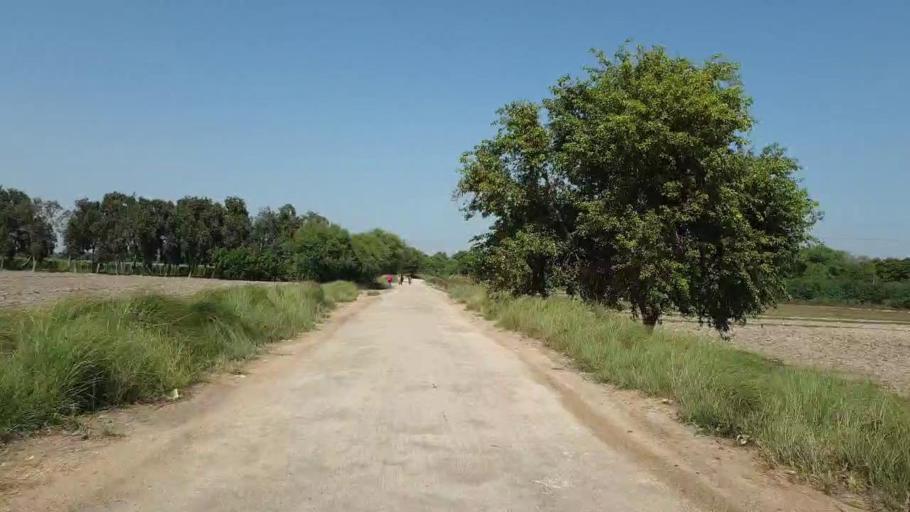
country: PK
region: Sindh
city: Tando Jam
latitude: 25.4268
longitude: 68.4591
